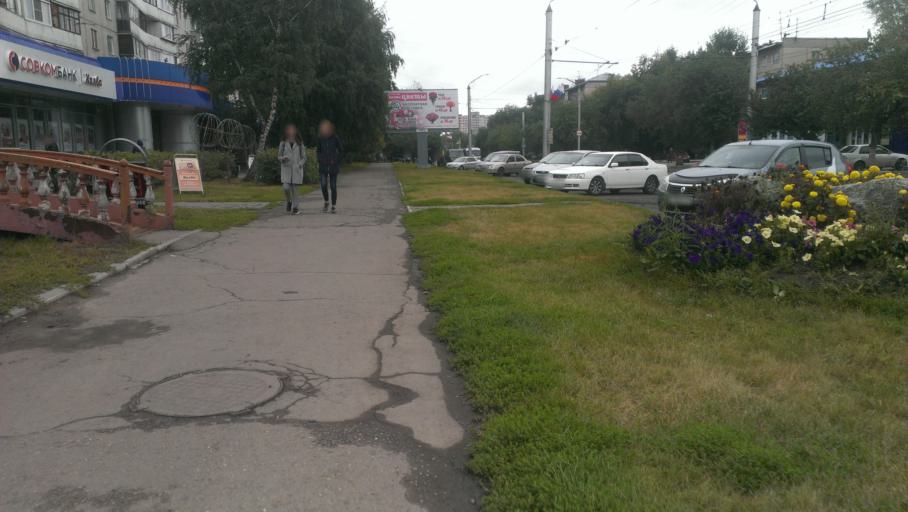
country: RU
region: Altai Krai
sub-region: Gorod Barnaulskiy
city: Barnaul
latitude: 53.3705
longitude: 83.6862
